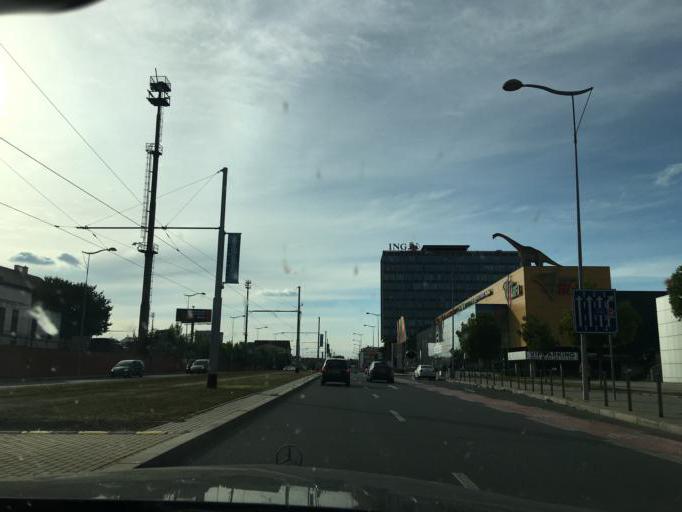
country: CZ
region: Praha
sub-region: Praha 9
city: Prosek
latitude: 50.1031
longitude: 14.4934
